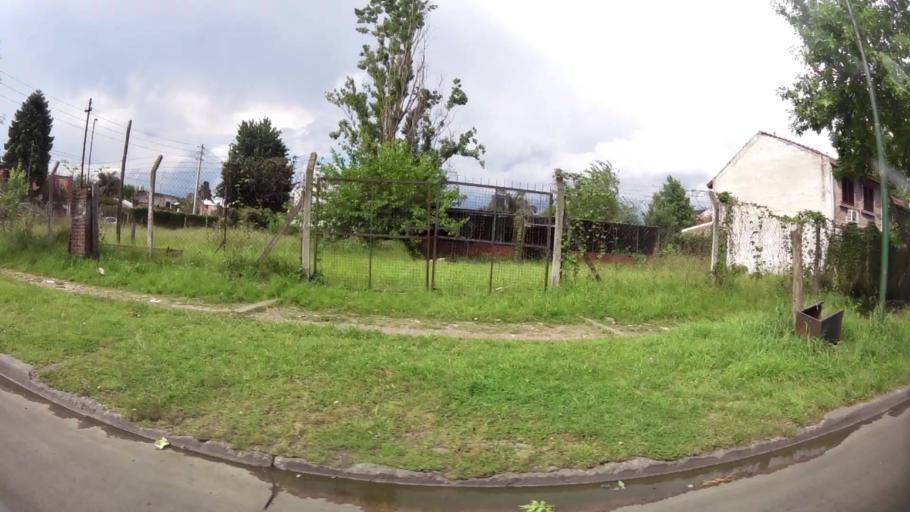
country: AR
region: Buenos Aires
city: Ituzaingo
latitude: -34.6483
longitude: -58.6867
